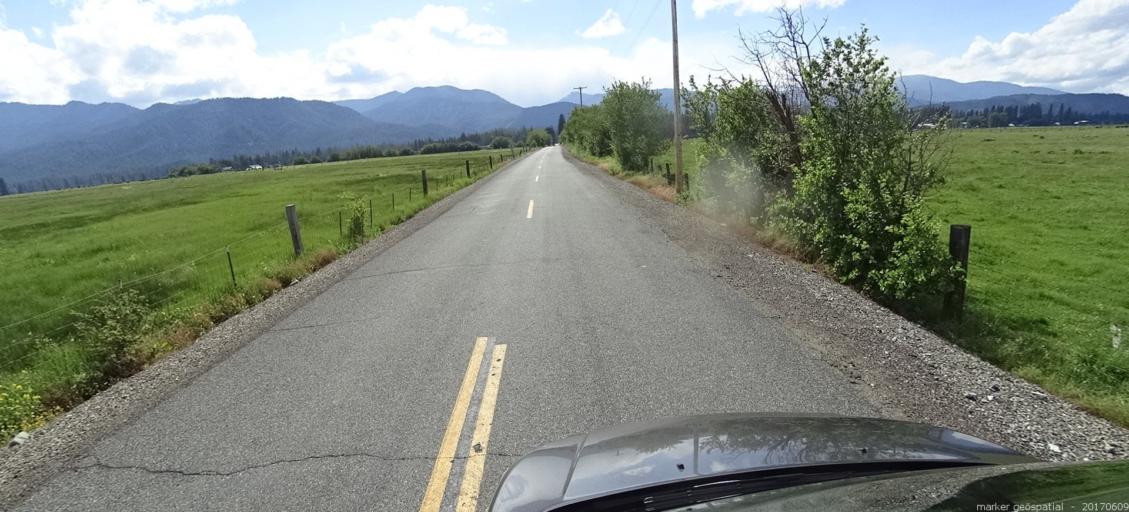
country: US
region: California
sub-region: Siskiyou County
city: Yreka
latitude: 41.5152
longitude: -122.8892
